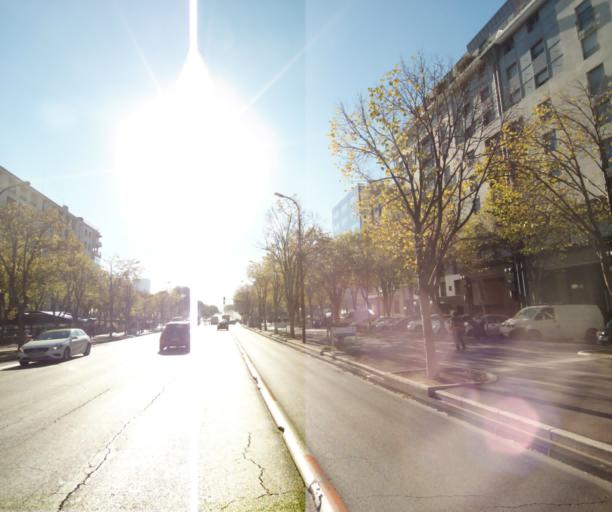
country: FR
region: Provence-Alpes-Cote d'Azur
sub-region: Departement des Bouches-du-Rhone
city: Marseille 08
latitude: 43.2738
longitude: 5.3905
